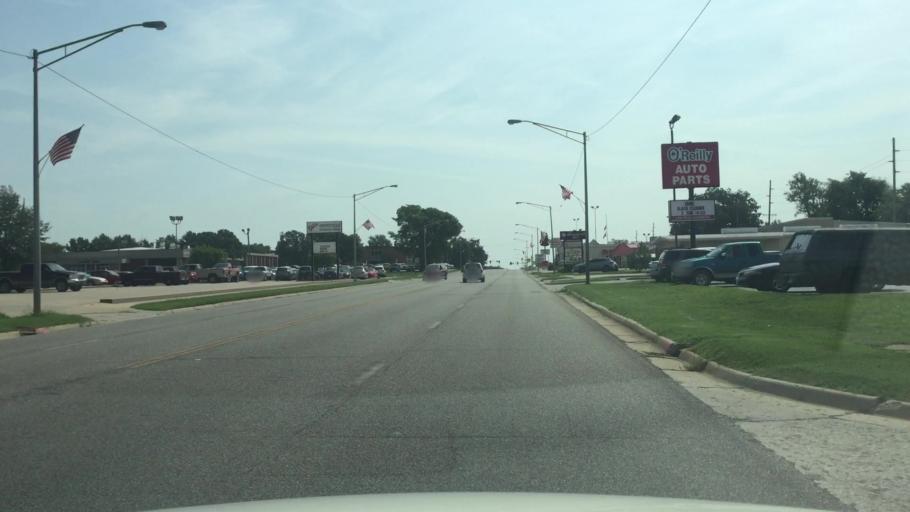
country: US
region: Kansas
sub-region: Montgomery County
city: Coffeyville
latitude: 37.0329
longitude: -95.6256
